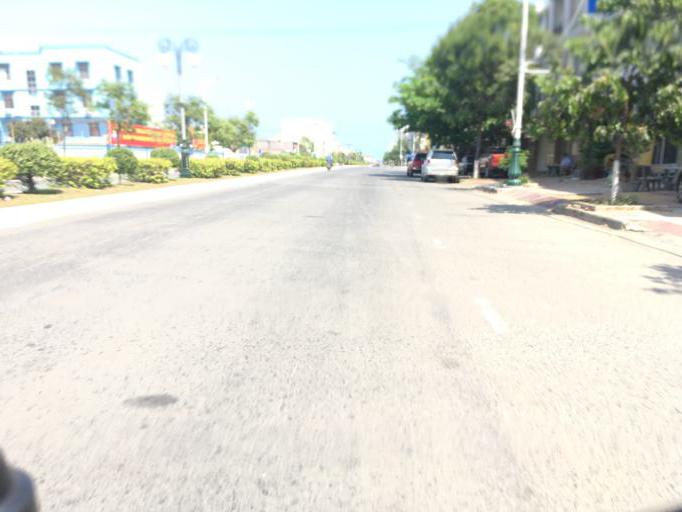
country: VN
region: Ninh Thuan
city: Phan Rang-Thap Cham
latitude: 11.5636
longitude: 109.0143
